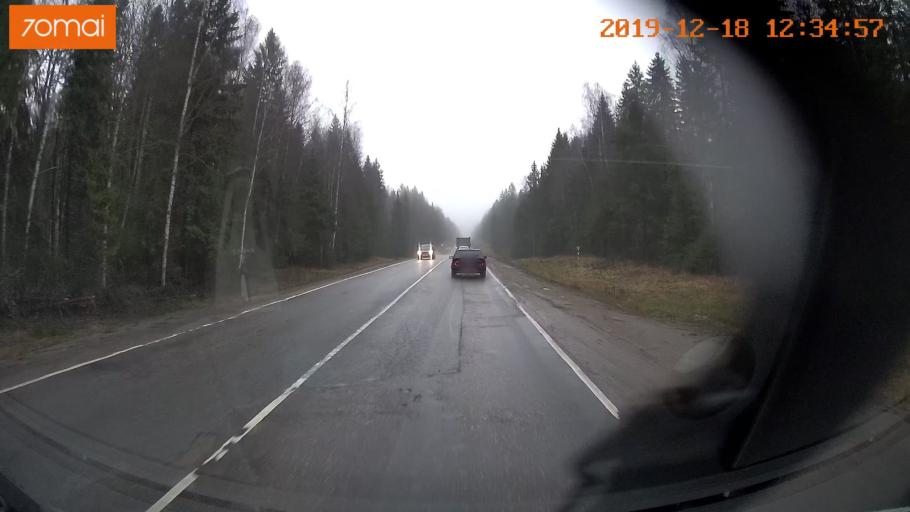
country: RU
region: Moskovskaya
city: Rumyantsevo
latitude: 56.1253
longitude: 36.5776
